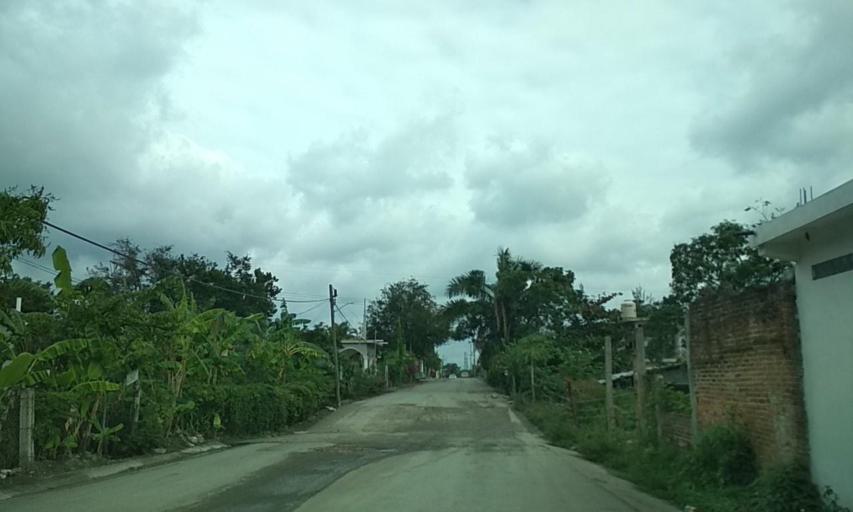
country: MX
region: Veracruz
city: Agua Dulce
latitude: 20.3619
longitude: -97.3333
